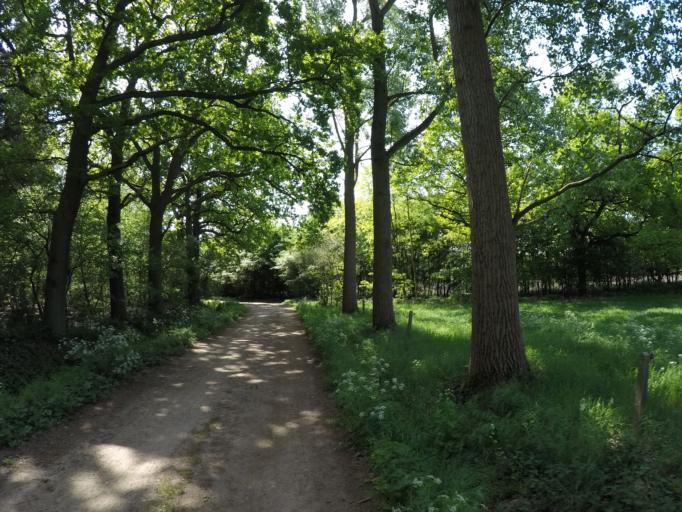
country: BE
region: Flanders
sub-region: Provincie Antwerpen
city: Oostmalle
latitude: 51.2729
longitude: 4.7426
